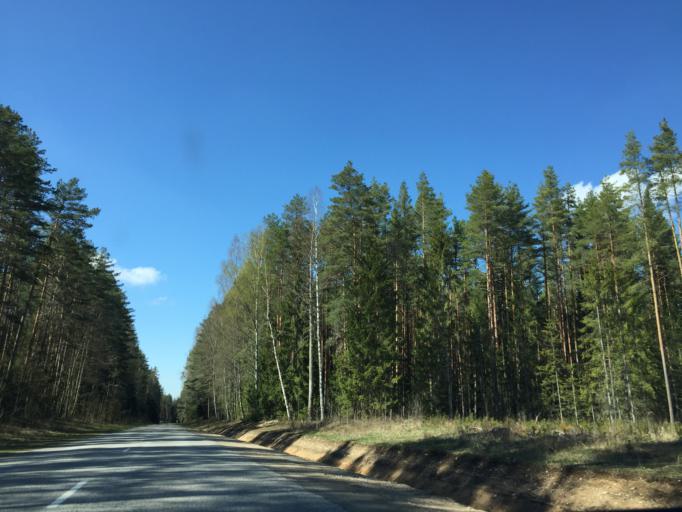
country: LV
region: Strenci
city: Strenci
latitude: 57.5961
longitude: 25.7249
